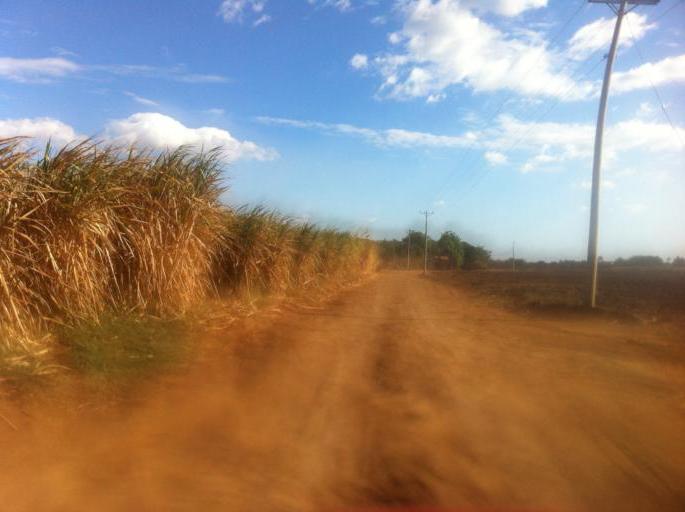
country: NI
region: Managua
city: Carlos Fonseca Amador
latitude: 11.9021
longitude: -86.5892
